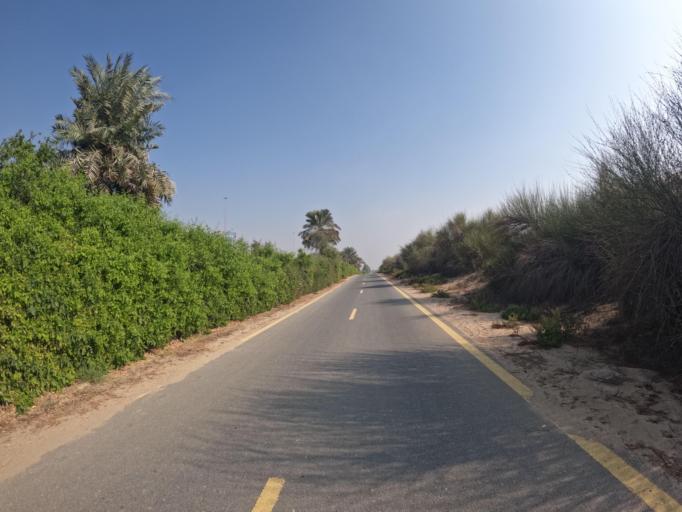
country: AE
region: Dubai
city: Dubai
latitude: 25.0832
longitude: 55.3156
